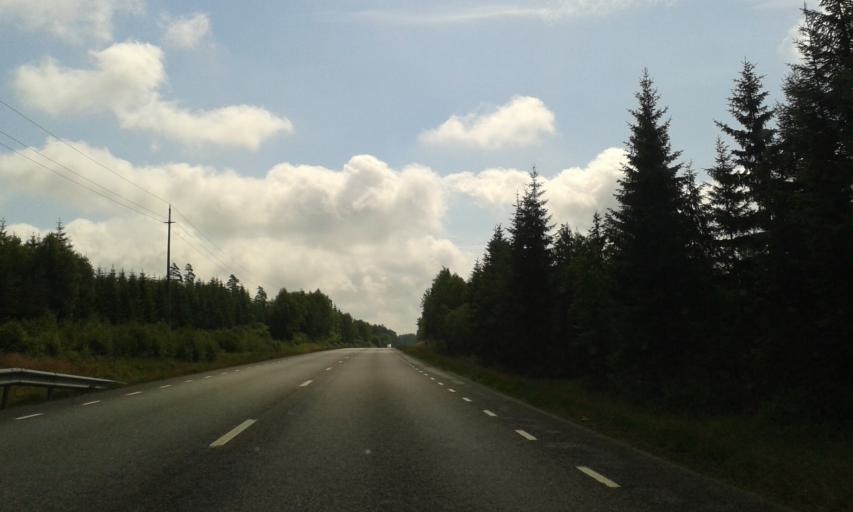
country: SE
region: Vaestra Goetaland
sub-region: Tranemo Kommun
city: Langhem
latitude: 57.6071
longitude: 13.1470
